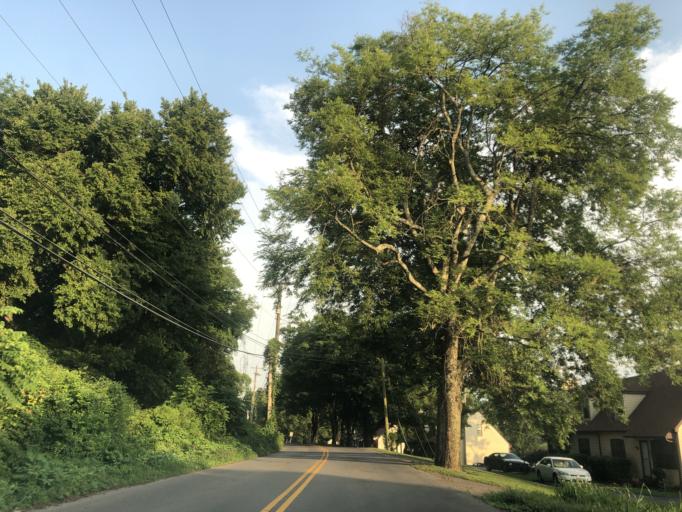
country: US
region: Tennessee
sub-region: Davidson County
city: Lakewood
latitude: 36.1410
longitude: -86.6371
